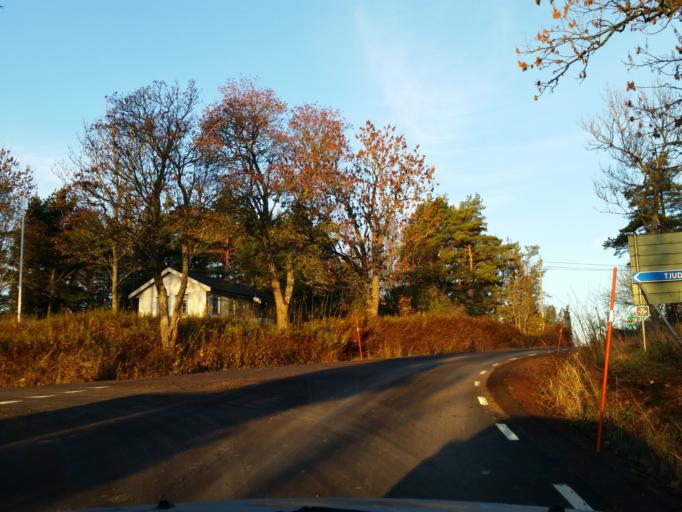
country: AX
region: Alands landsbygd
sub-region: Sund
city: Sund
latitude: 60.2352
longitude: 20.0763
